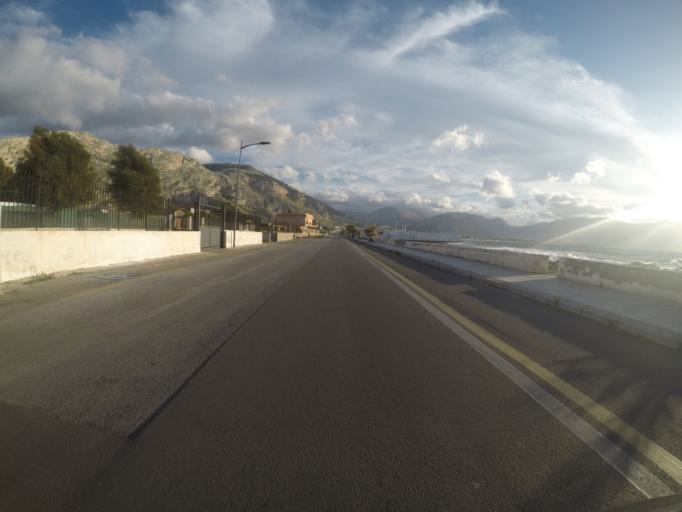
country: IT
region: Sicily
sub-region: Palermo
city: Isola delle Femmine
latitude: 38.1980
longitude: 13.2437
